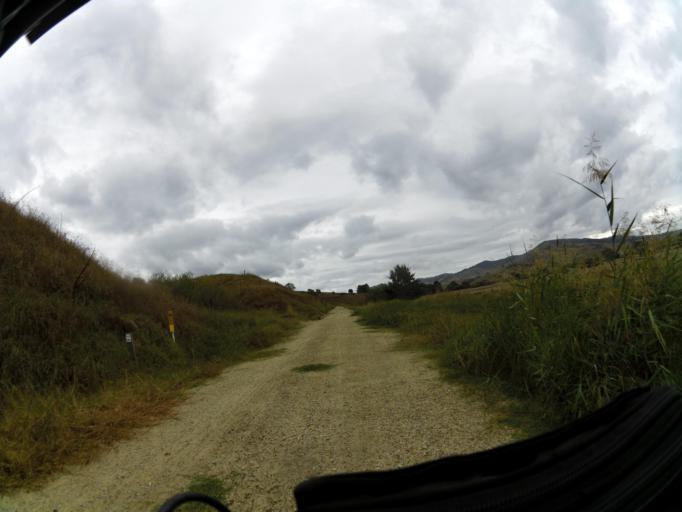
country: AU
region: New South Wales
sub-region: Albury Municipality
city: East Albury
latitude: -36.1922
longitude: 147.2971
